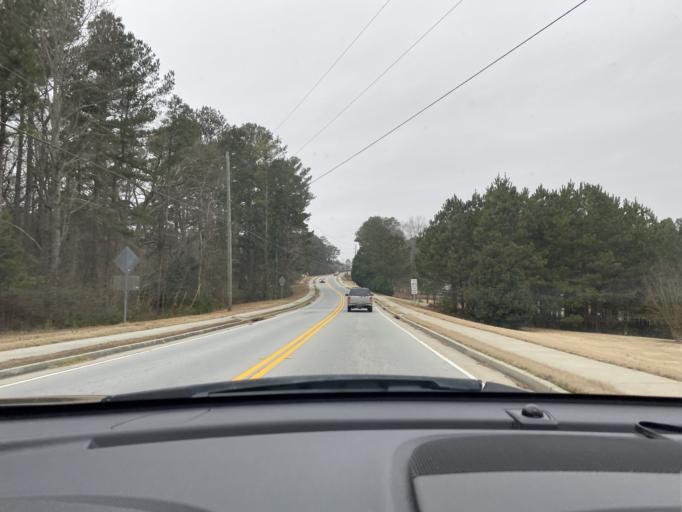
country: US
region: Georgia
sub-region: Gwinnett County
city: Grayson
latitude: 33.9168
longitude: -83.8996
